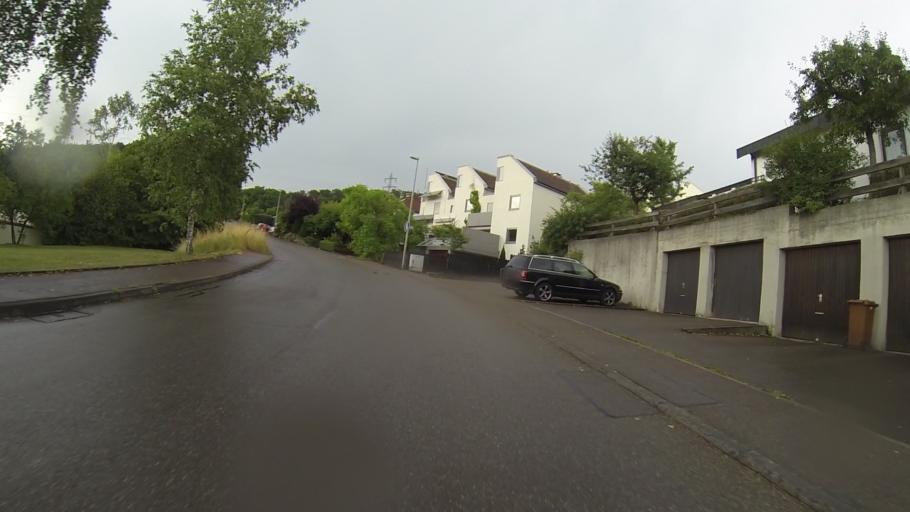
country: DE
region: Baden-Wuerttemberg
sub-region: Regierungsbezirk Stuttgart
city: Heidenheim an der Brenz
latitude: 48.6773
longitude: 10.1765
